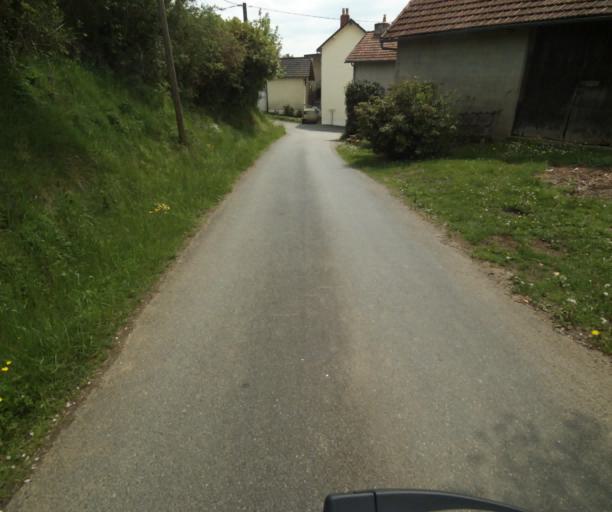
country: FR
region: Limousin
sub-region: Departement de la Correze
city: Tulle
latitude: 45.2804
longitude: 1.7605
